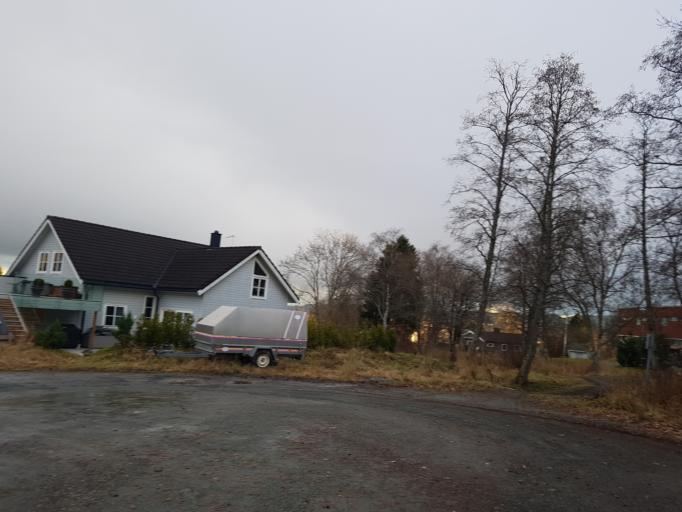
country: NO
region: Sor-Trondelag
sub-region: Trondheim
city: Trondheim
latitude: 63.4148
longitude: 10.3589
